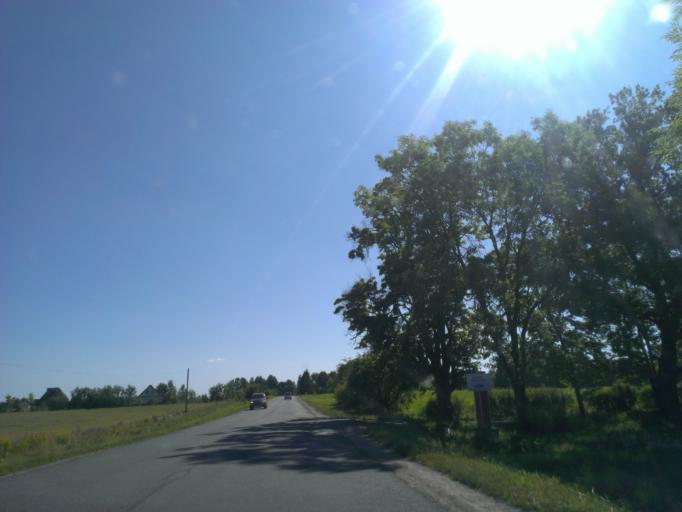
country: LV
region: Sigulda
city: Sigulda
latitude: 57.1400
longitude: 24.8433
